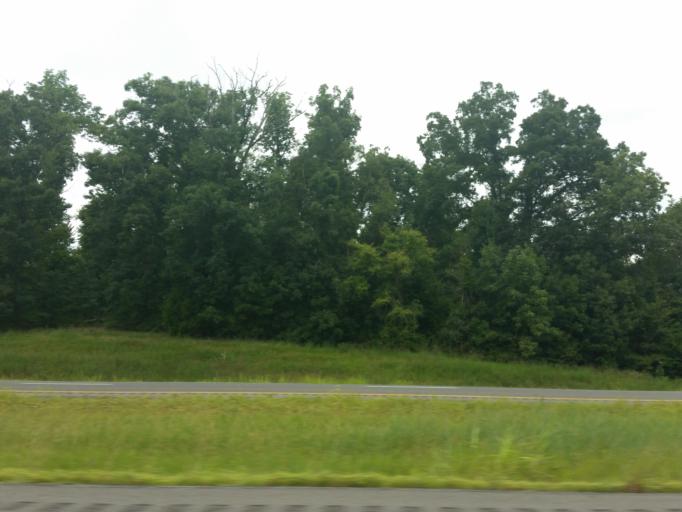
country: US
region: Kentucky
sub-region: Lyon County
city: Eddyville
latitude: 37.0699
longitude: -88.0808
